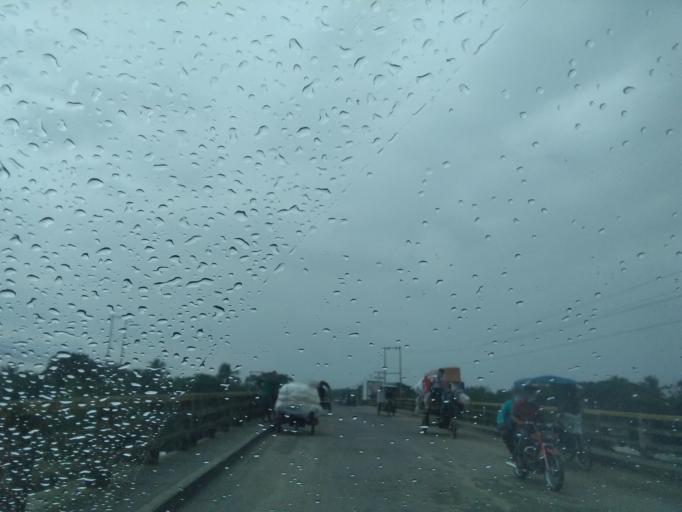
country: IN
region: West Bengal
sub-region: North 24 Parganas
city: Taki
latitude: 22.4580
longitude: 89.0337
